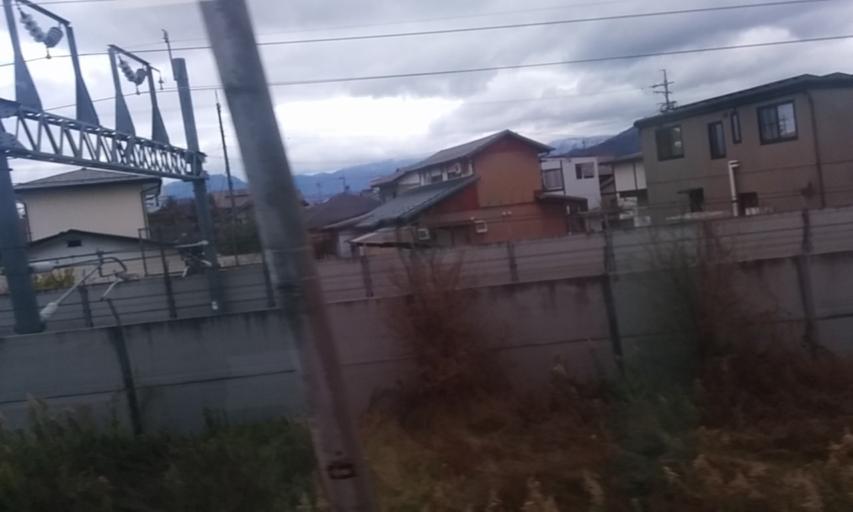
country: JP
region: Nagano
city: Nagano-shi
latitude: 36.5719
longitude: 138.1360
